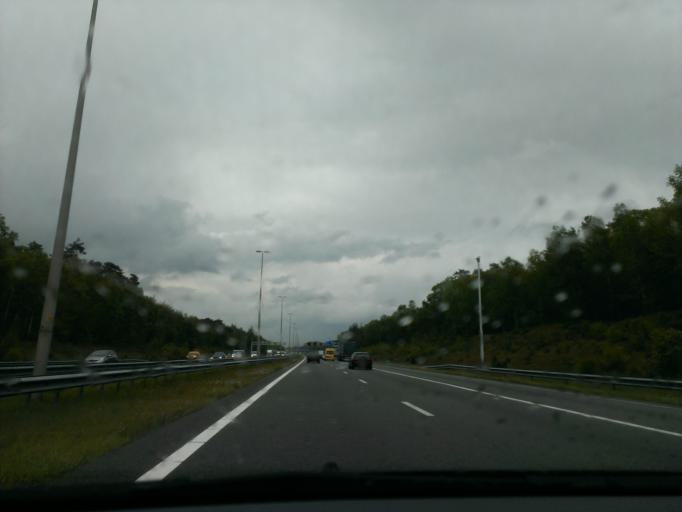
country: NL
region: Gelderland
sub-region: Gemeente Apeldoorn
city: Beekbergen
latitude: 52.1304
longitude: 5.9709
